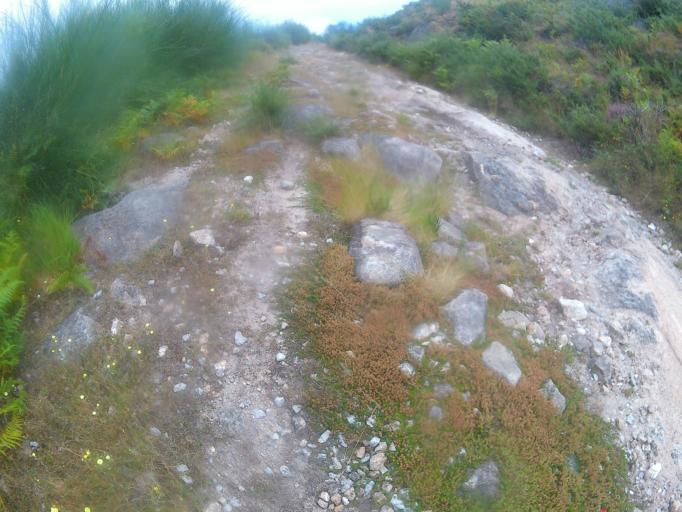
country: PT
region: Viana do Castelo
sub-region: Ponte de Lima
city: Ponte de Lima
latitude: 41.7202
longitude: -8.6021
